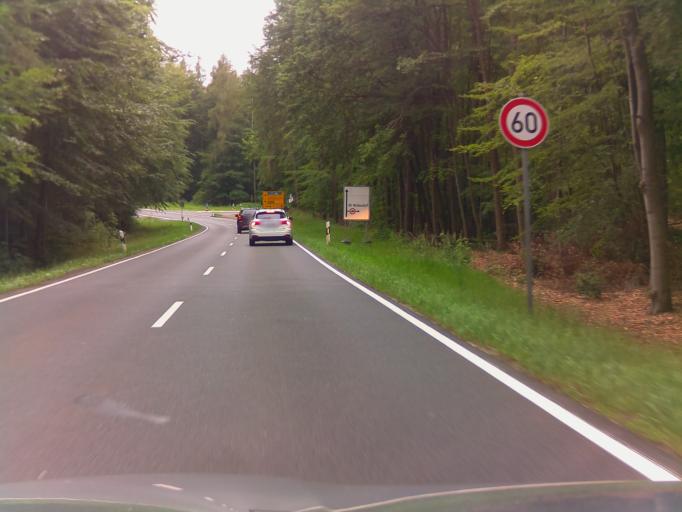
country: DE
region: Bavaria
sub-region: Regierungsbezirk Unterfranken
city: Rothenbuch
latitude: 49.9754
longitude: 9.3619
